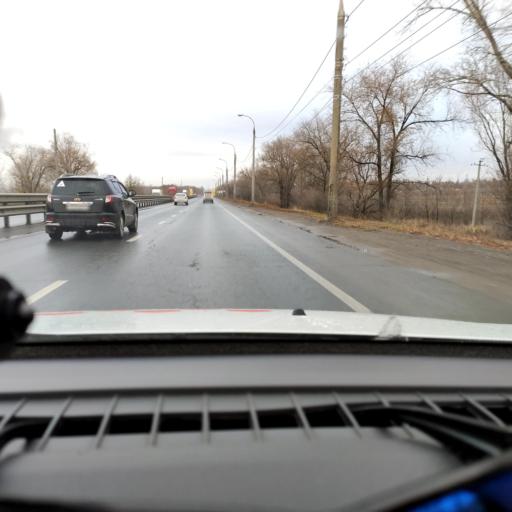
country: RU
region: Samara
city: Samara
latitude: 53.1194
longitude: 50.1681
